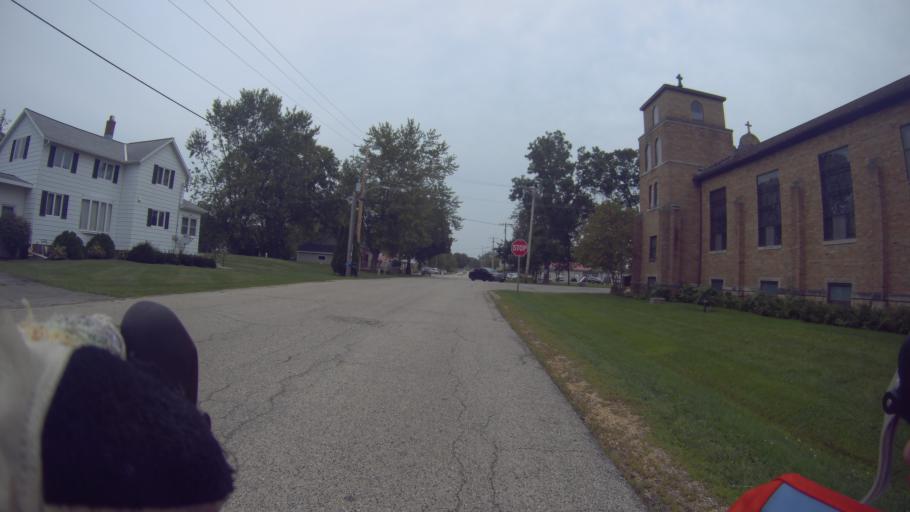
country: US
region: Wisconsin
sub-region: Dane County
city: Verona
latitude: 42.9295
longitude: -89.5274
